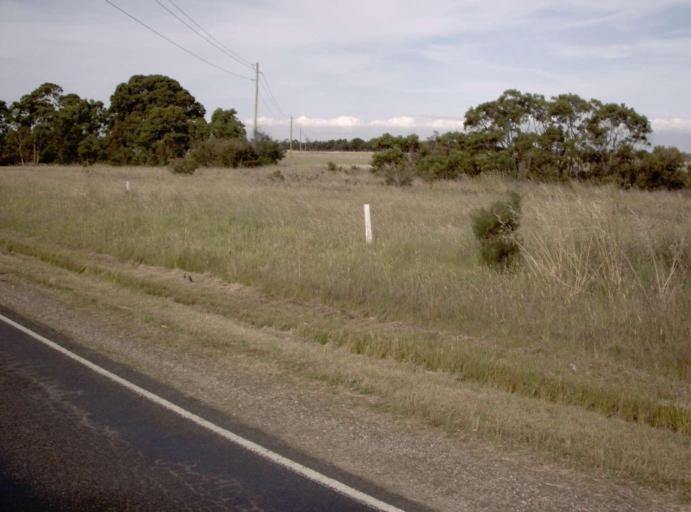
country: AU
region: Victoria
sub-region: Latrobe
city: Traralgon
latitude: -38.0760
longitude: 146.6112
